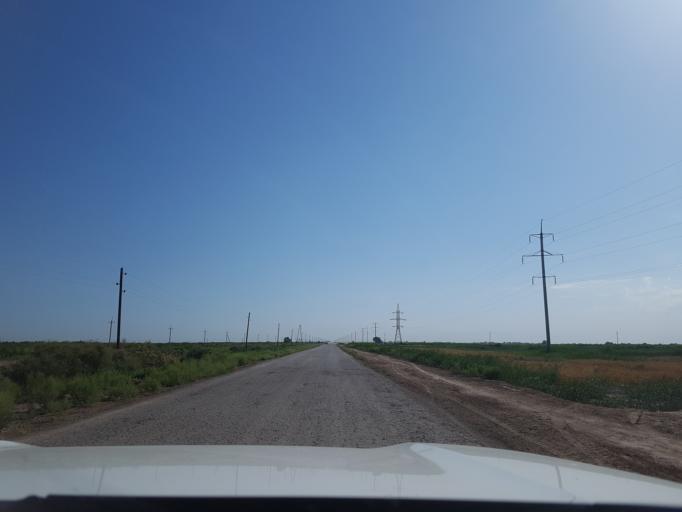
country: TM
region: Dasoguz
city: Koeneuergench
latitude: 42.1079
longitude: 58.9131
